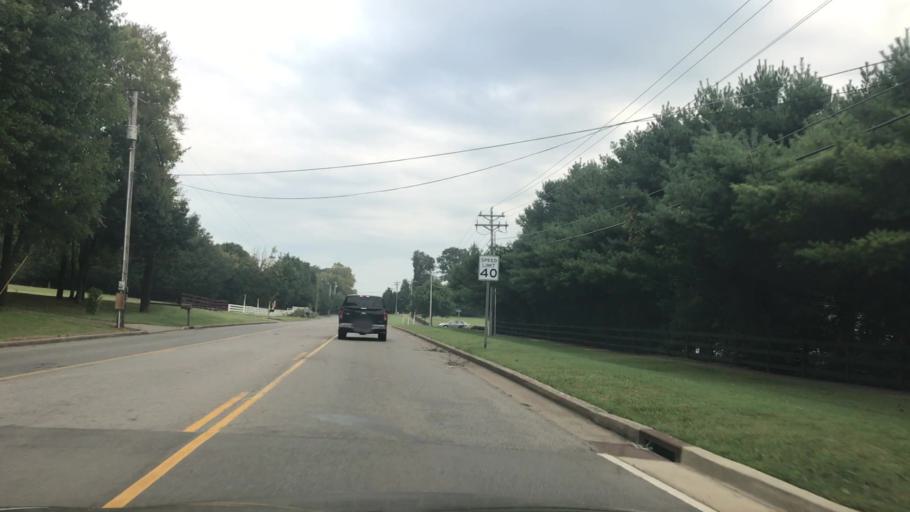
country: US
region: Tennessee
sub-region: Williamson County
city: Franklin
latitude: 35.8988
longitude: -86.8256
